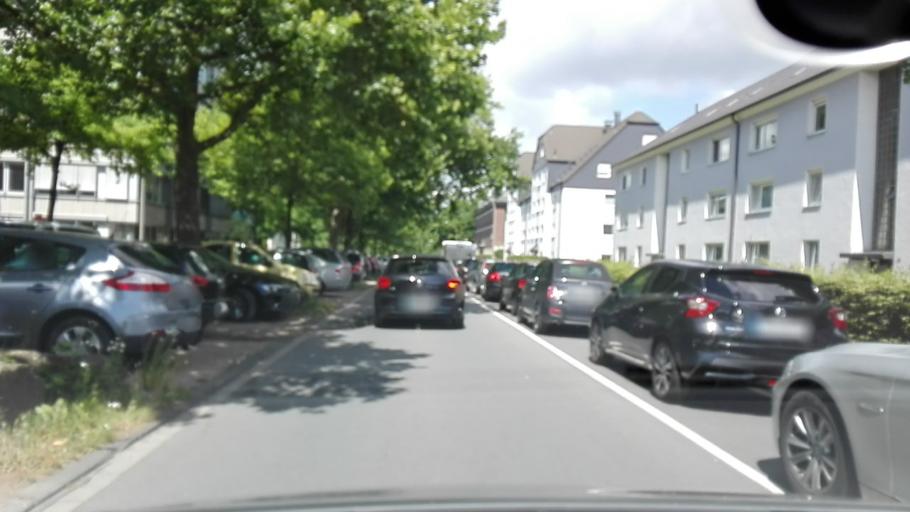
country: DE
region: North Rhine-Westphalia
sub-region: Regierungsbezirk Arnsberg
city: Dortmund
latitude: 51.5032
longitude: 7.4832
